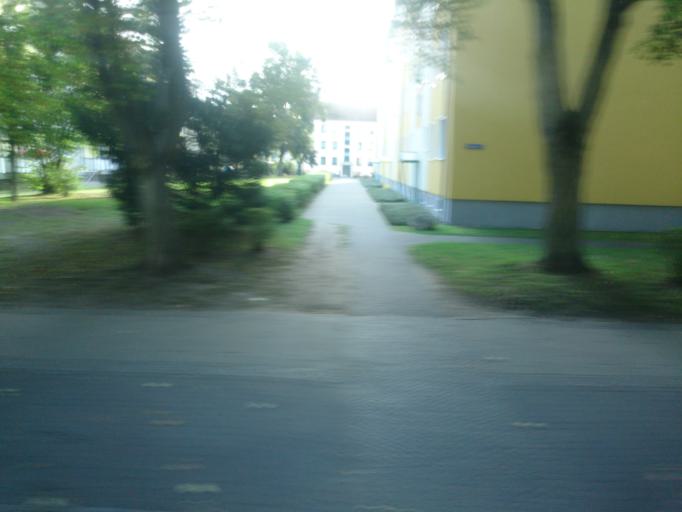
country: DE
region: Mecklenburg-Vorpommern
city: Anklam
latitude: 53.8576
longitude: 13.6888
